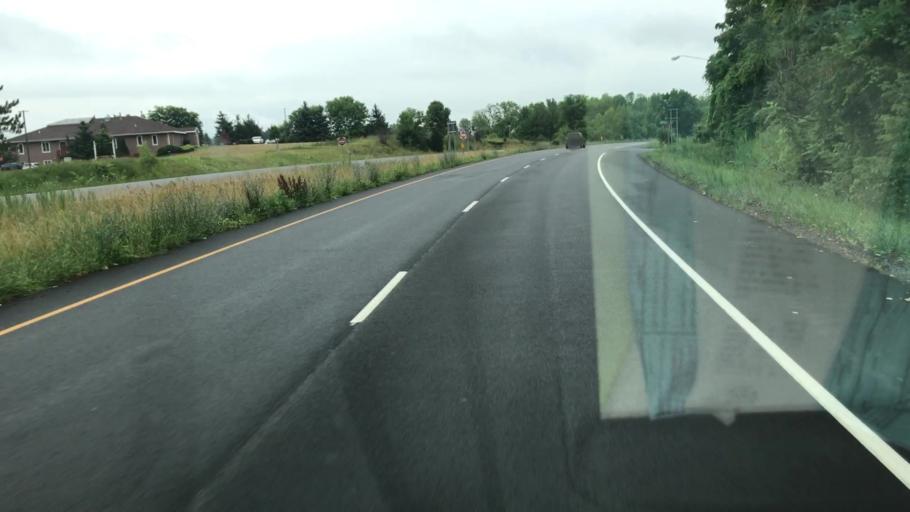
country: US
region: New York
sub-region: Onondaga County
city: Liverpool
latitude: 43.1376
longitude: -76.2081
